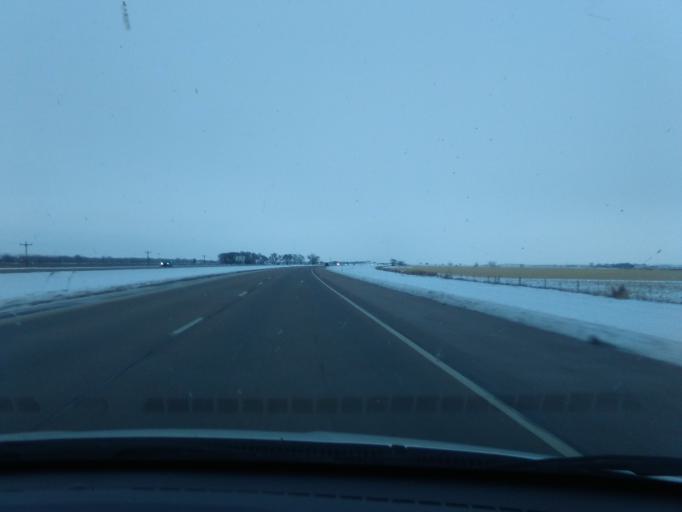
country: US
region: Nebraska
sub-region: Keith County
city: Ogallala
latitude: 41.1200
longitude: -101.6838
